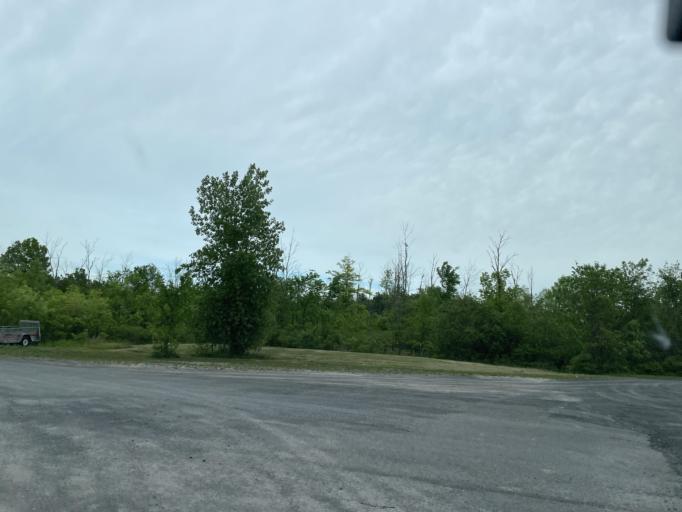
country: US
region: New York
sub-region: Ulster County
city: Saugerties
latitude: 42.0969
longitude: -73.9493
